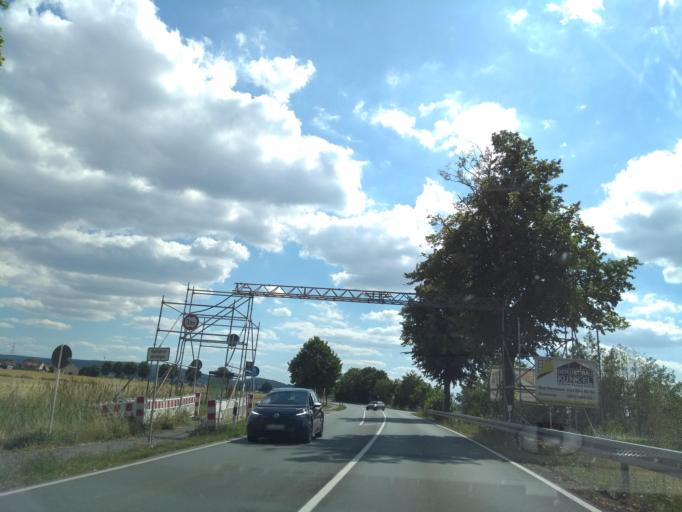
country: DE
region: Lower Saxony
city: Hohnhorst
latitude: 52.3697
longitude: 9.3823
